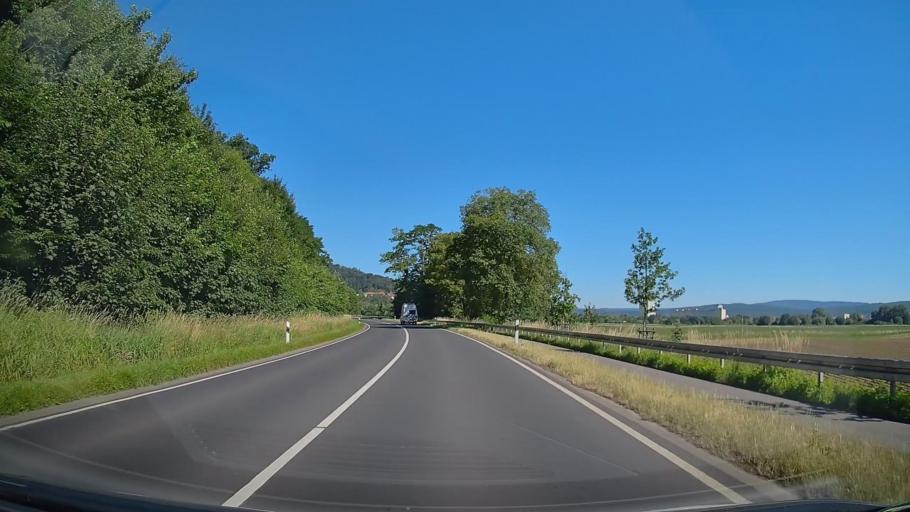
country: DE
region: Lower Saxony
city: Hameln
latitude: 52.0818
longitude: 9.3597
